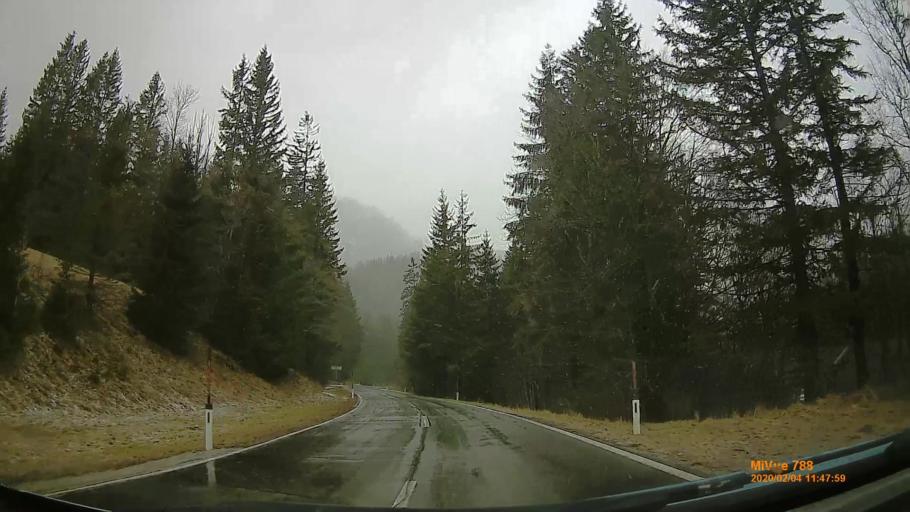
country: AT
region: Styria
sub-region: Politischer Bezirk Bruck-Muerzzuschlag
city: Muerzsteg
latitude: 47.7148
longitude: 15.4778
